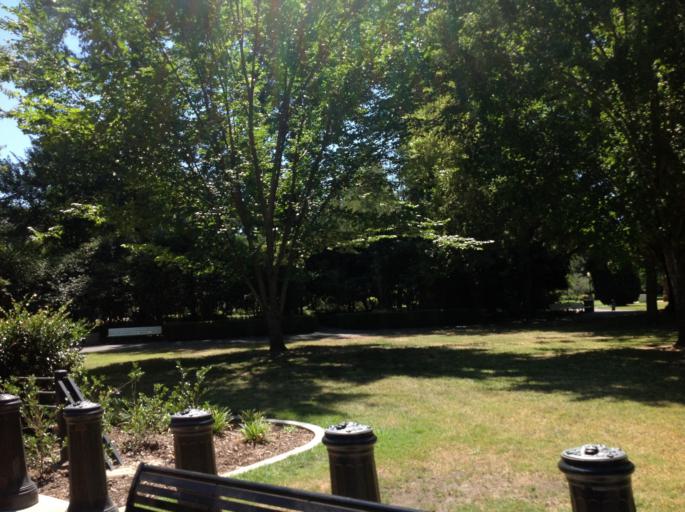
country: US
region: California
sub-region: Sacramento County
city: Sacramento
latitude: 38.5768
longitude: -121.4914
